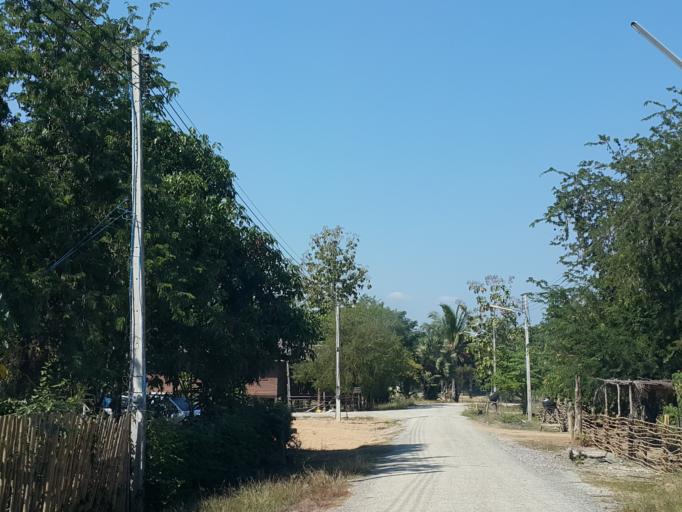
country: TH
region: Sukhothai
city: Thung Saliam
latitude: 17.3440
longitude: 99.4427
